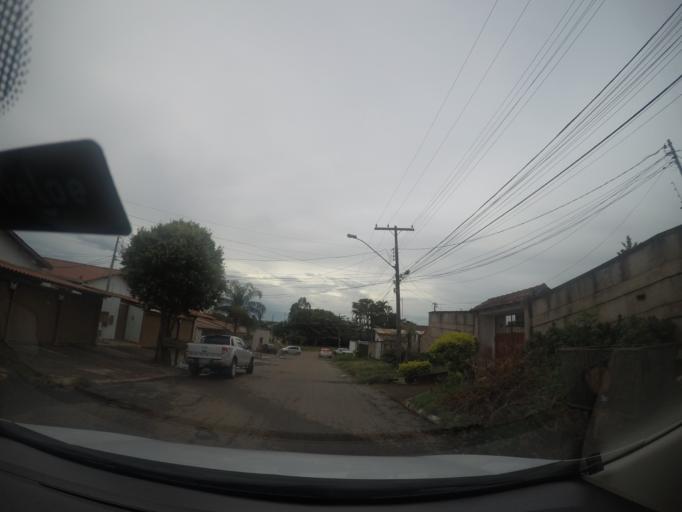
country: BR
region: Goias
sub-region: Goiania
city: Goiania
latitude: -16.6361
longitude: -49.2422
